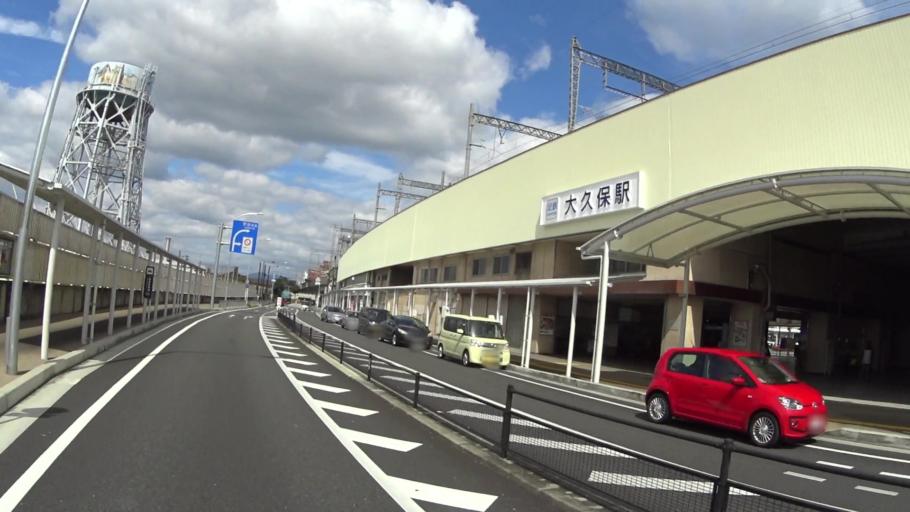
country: JP
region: Kyoto
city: Uji
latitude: 34.8741
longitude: 135.7767
